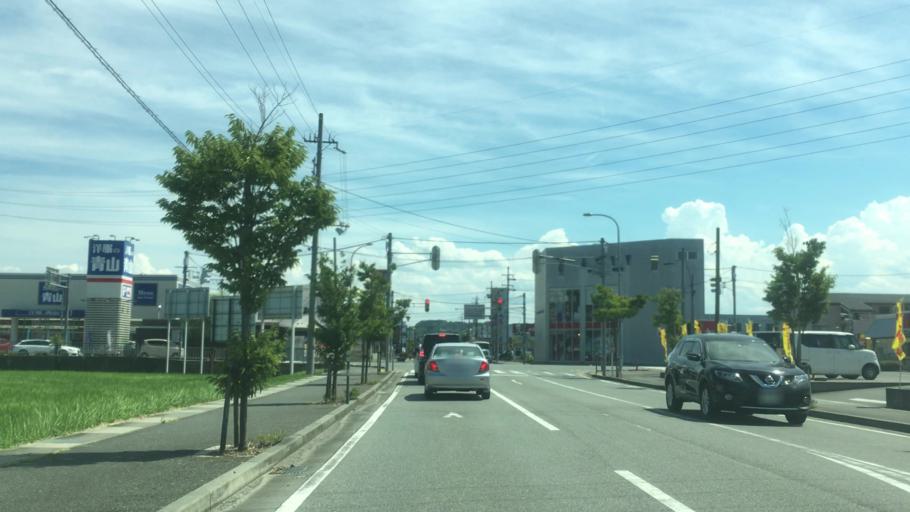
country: JP
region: Hyogo
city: Toyooka
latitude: 35.5548
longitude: 134.8156
